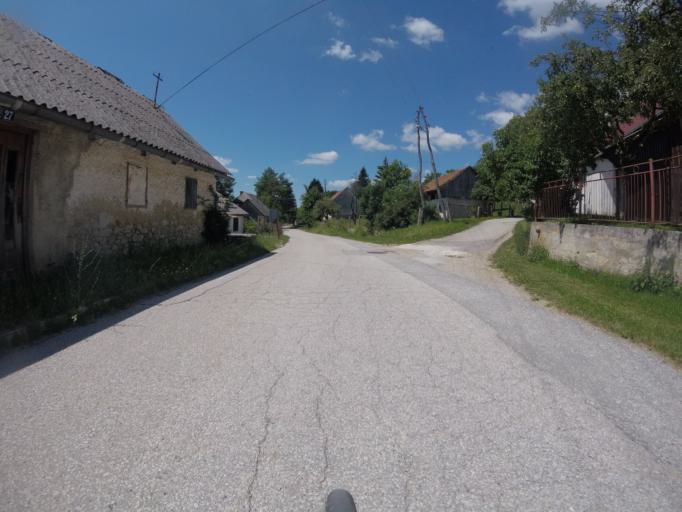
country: SI
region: Kostanjevica na Krki
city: Kostanjevica na Krki
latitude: 45.7722
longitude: 15.4678
